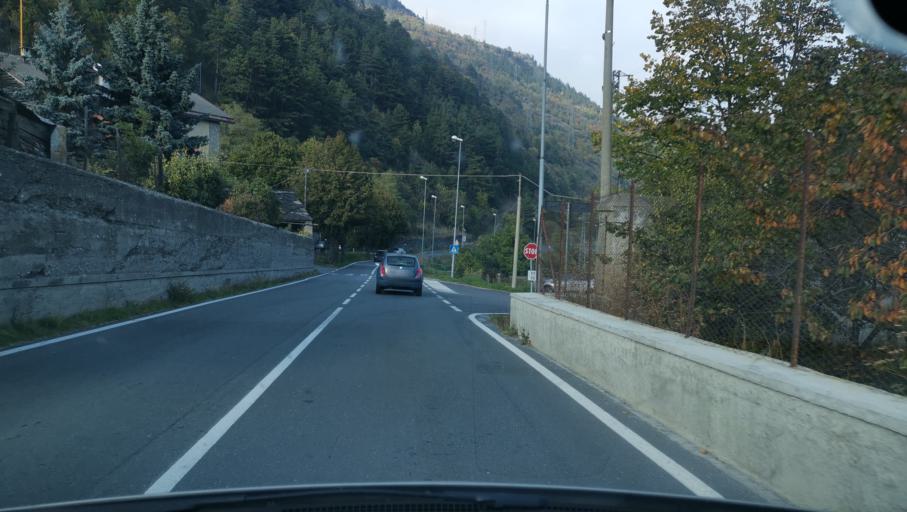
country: IT
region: Piedmont
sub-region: Provincia di Torino
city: Salbertrand
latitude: 45.0728
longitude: 6.8849
